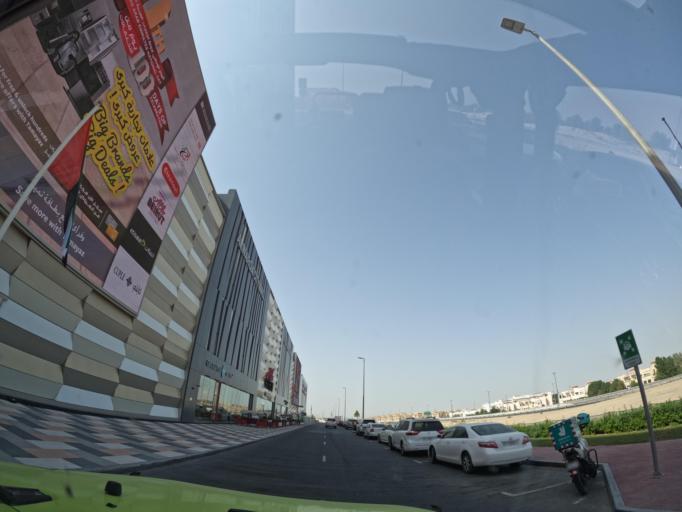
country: AE
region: Ash Shariqah
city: Sharjah
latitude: 25.2067
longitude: 55.4264
